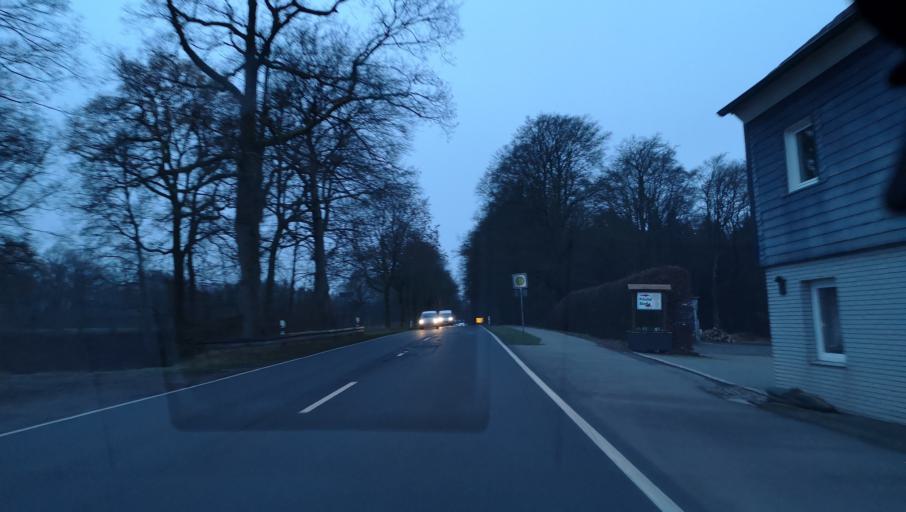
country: DE
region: North Rhine-Westphalia
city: Radevormwald
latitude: 51.2154
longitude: 7.3892
